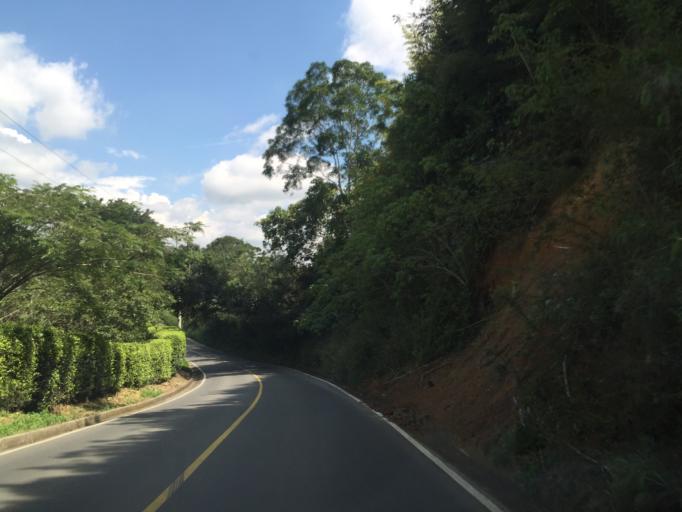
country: CO
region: Valle del Cauca
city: Ulloa
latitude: 4.7374
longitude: -75.7881
